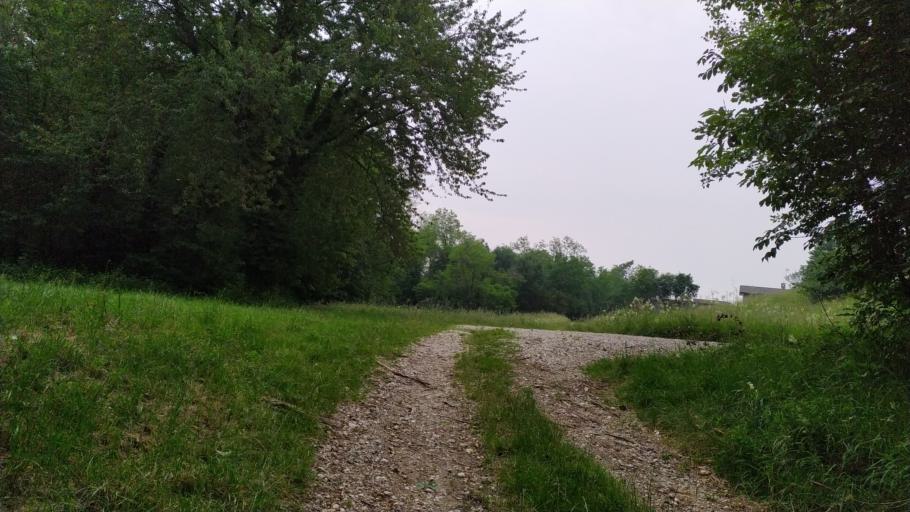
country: IT
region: Friuli Venezia Giulia
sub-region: Provincia di Udine
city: Majano
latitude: 46.1863
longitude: 13.0351
